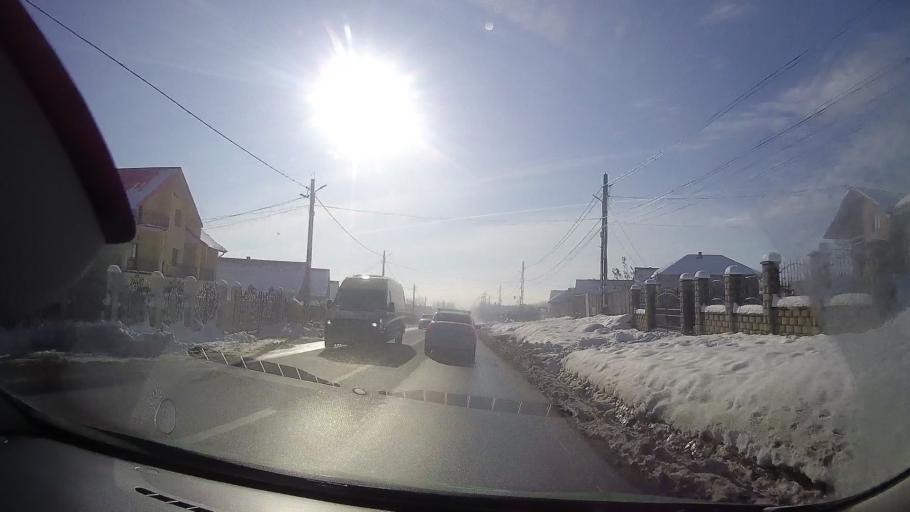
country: RO
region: Iasi
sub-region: Comuna Motca
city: Motca
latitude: 47.2534
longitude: 26.6099
